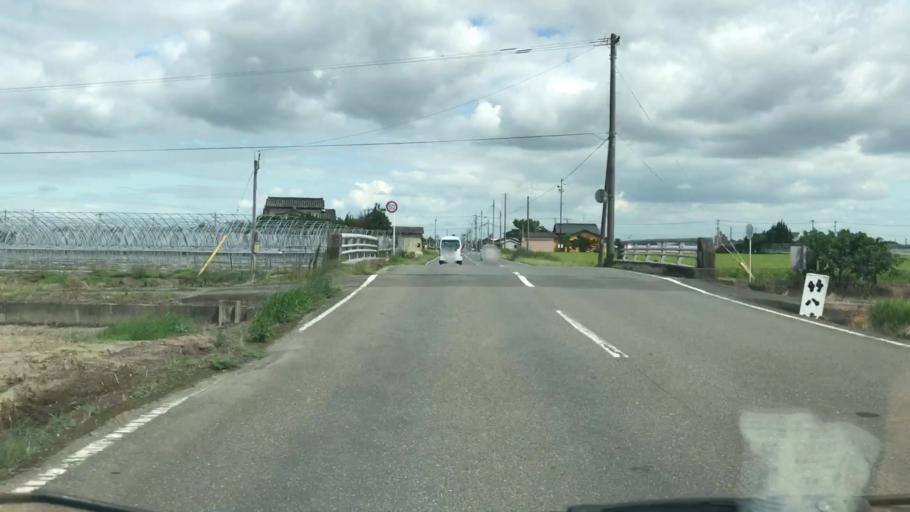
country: JP
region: Saga Prefecture
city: Saga-shi
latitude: 33.1957
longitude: 130.1840
